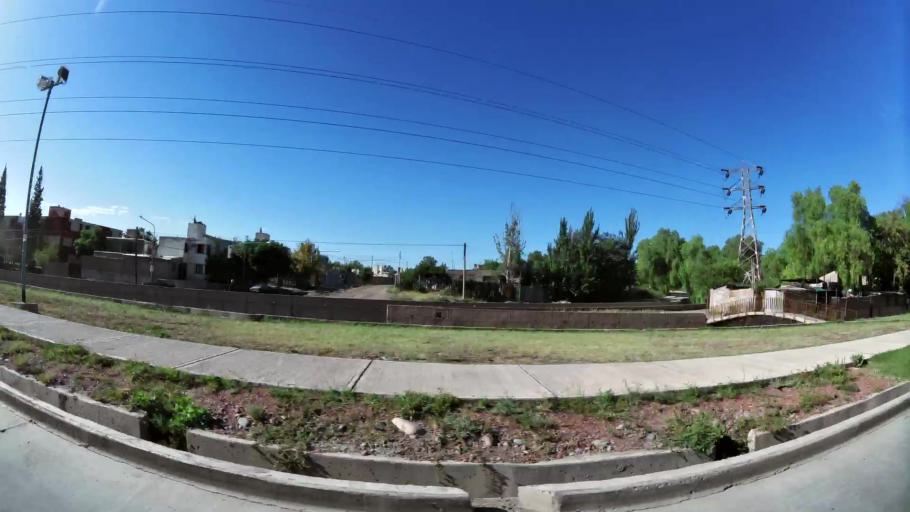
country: AR
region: Mendoza
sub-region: Departamento de Godoy Cruz
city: Godoy Cruz
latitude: -32.9250
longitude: -68.8672
